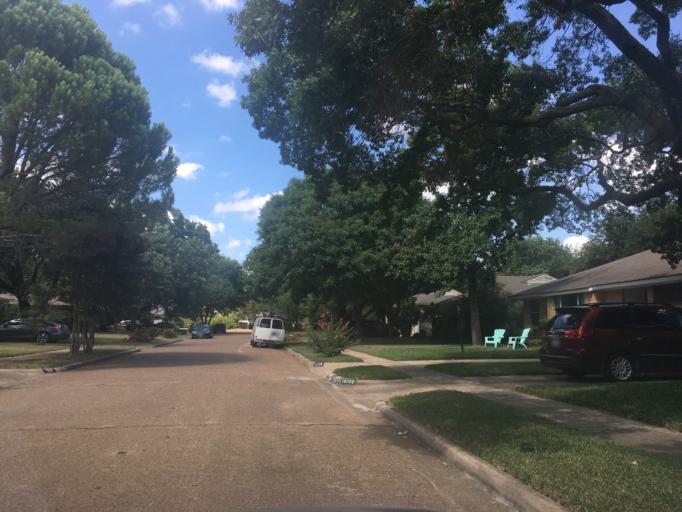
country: US
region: Texas
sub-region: Dallas County
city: Garland
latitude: 32.8324
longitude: -96.6789
